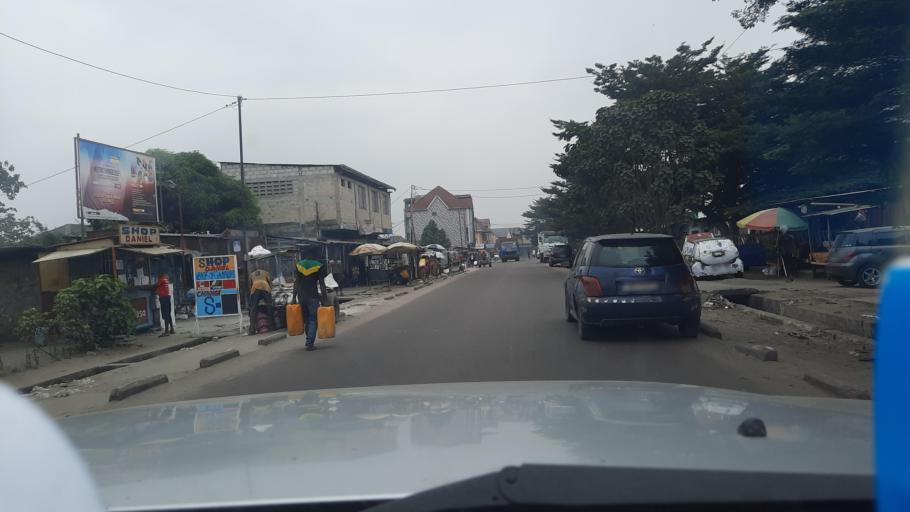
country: CD
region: Kinshasa
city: Masina
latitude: -4.3818
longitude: 15.3457
